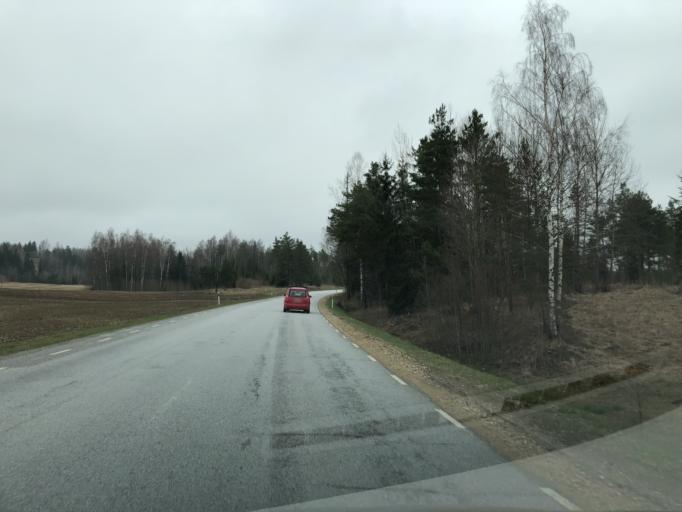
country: EE
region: Laeaene-Virumaa
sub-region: Rakke vald
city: Rakke
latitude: 58.9734
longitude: 26.2680
